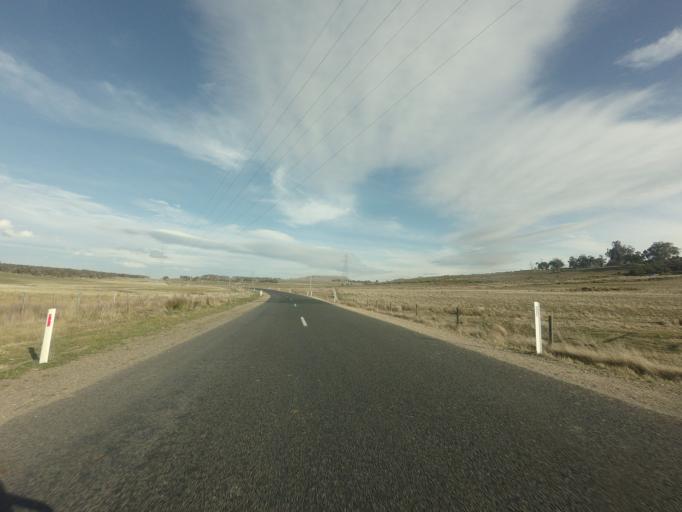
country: AU
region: Tasmania
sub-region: Derwent Valley
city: New Norfolk
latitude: -42.2610
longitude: 146.9376
